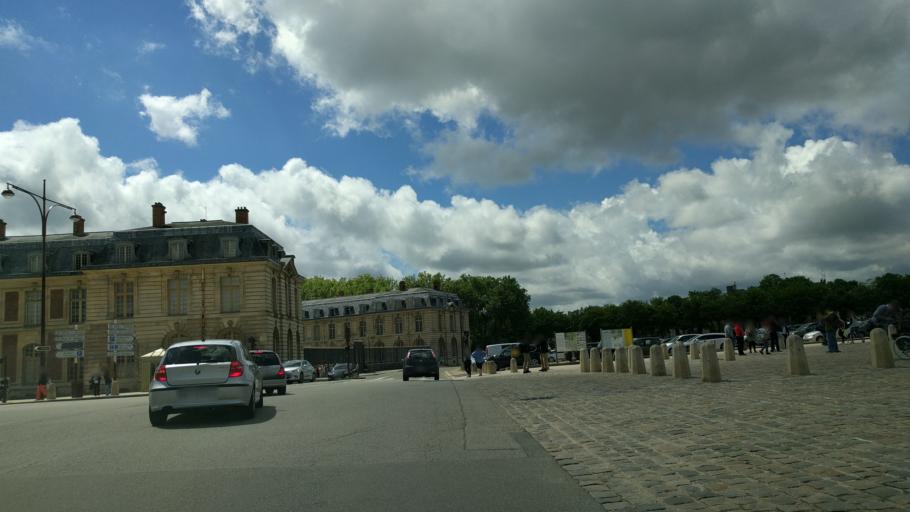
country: FR
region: Ile-de-France
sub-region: Departement des Yvelines
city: Versailles
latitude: 48.8034
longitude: 2.1265
